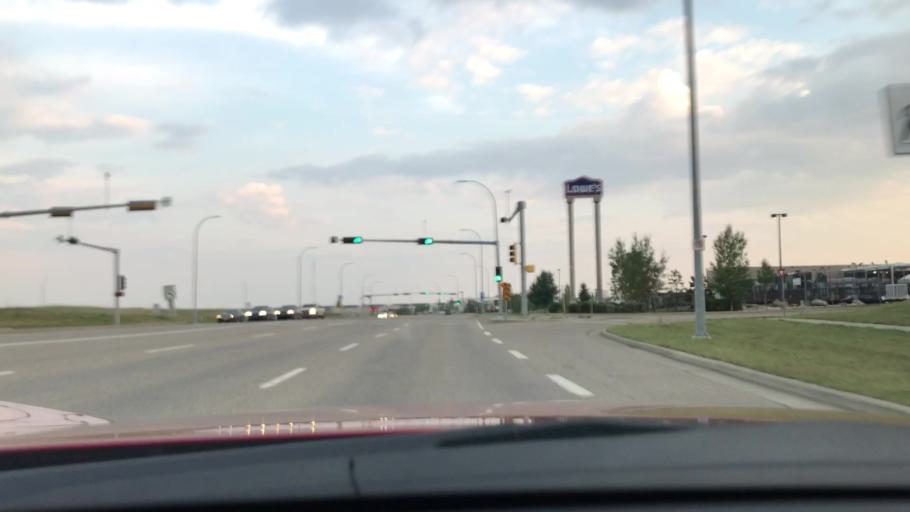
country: CA
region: Alberta
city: Airdrie
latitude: 51.2102
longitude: -113.9905
